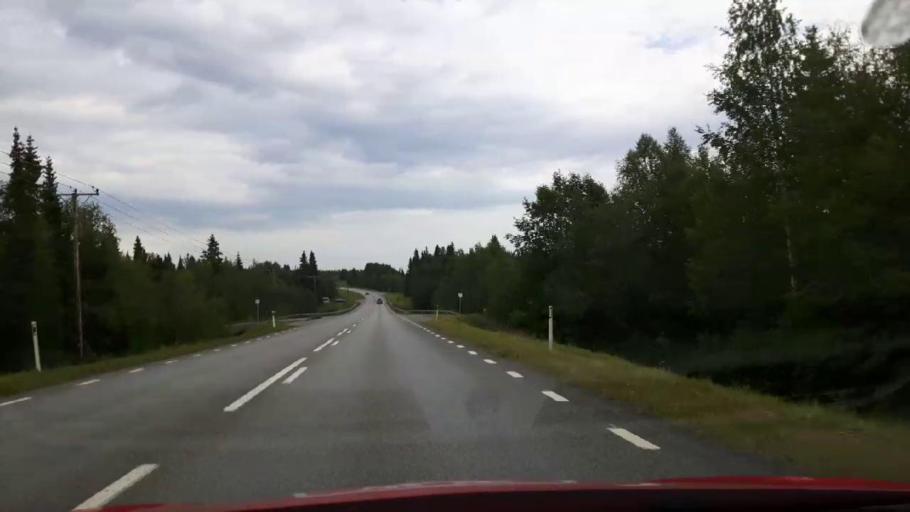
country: SE
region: Jaemtland
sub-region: Stroemsunds Kommun
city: Stroemsund
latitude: 63.6381
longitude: 15.3639
